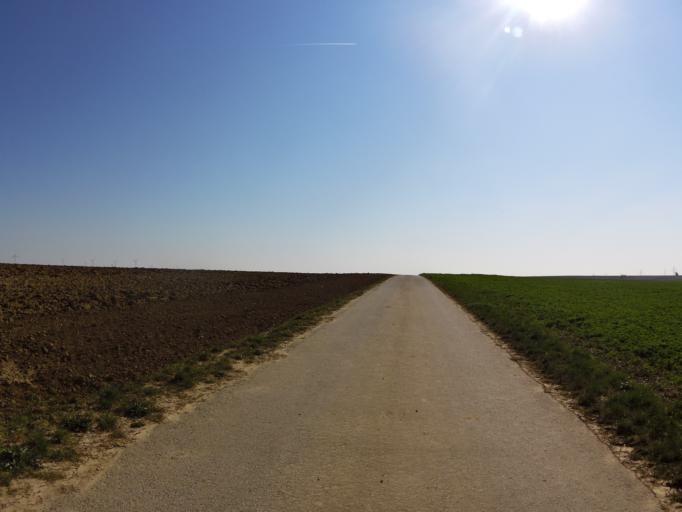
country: DE
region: Bavaria
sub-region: Regierungsbezirk Unterfranken
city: Biebelried
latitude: 49.8149
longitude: 10.1008
